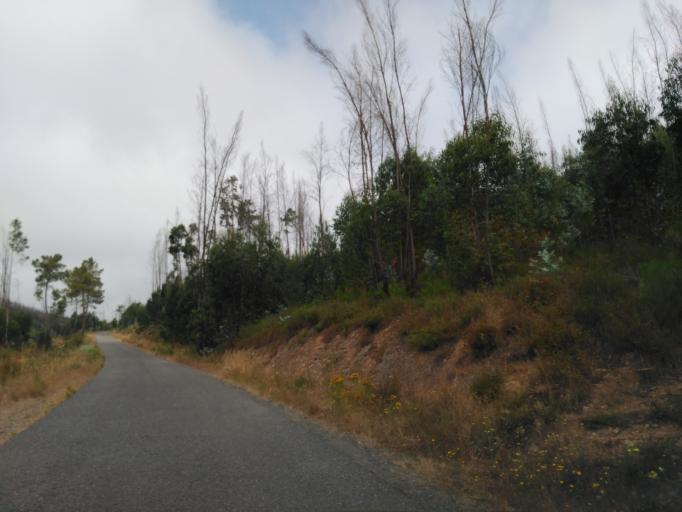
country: PT
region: Santarem
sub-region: Macao
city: Macao
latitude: 39.5880
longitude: -8.0621
